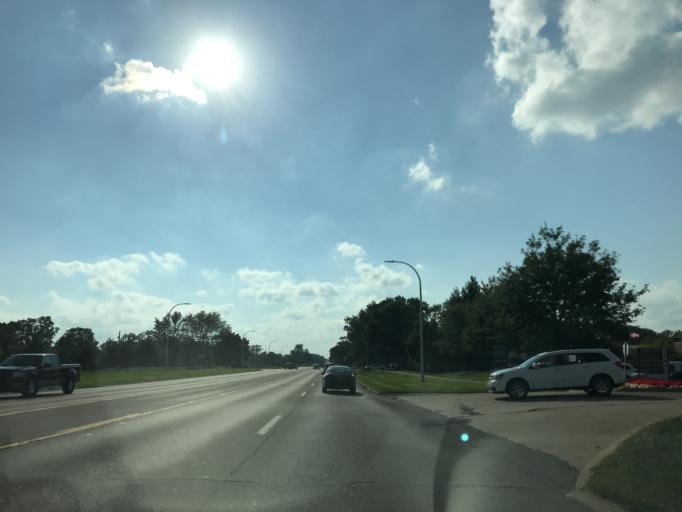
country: US
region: Michigan
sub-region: Wayne County
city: Livonia
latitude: 42.3966
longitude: -83.4045
